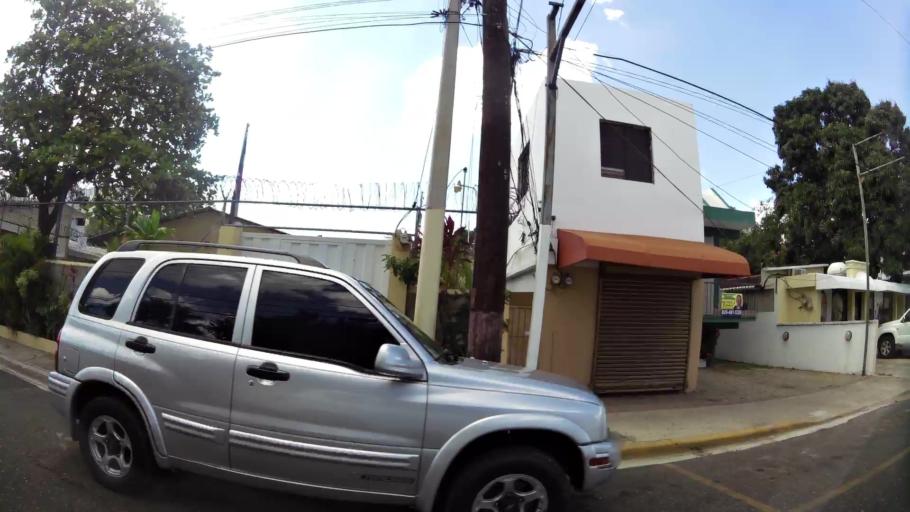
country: DO
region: Santiago
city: Santiago de los Caballeros
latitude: 19.4557
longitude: -70.6785
